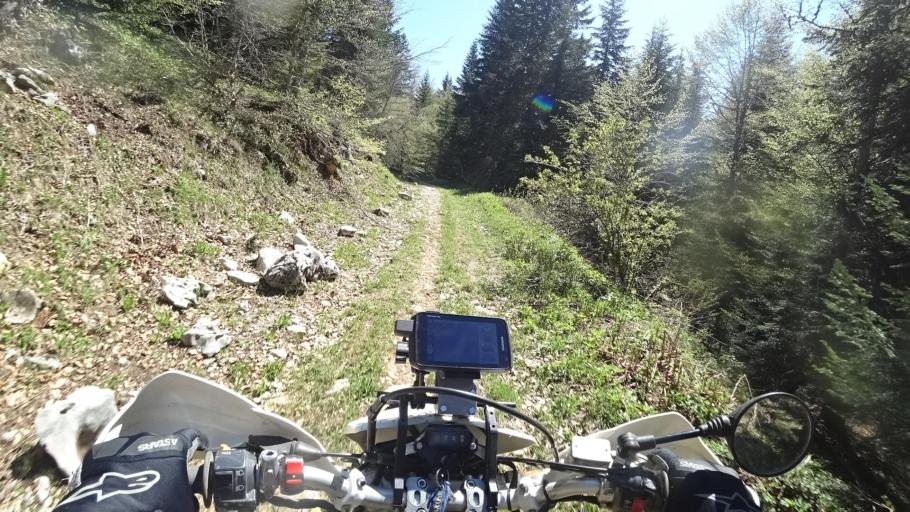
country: BA
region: Federation of Bosnia and Herzegovina
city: Rumboci
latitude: 43.8661
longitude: 17.4848
